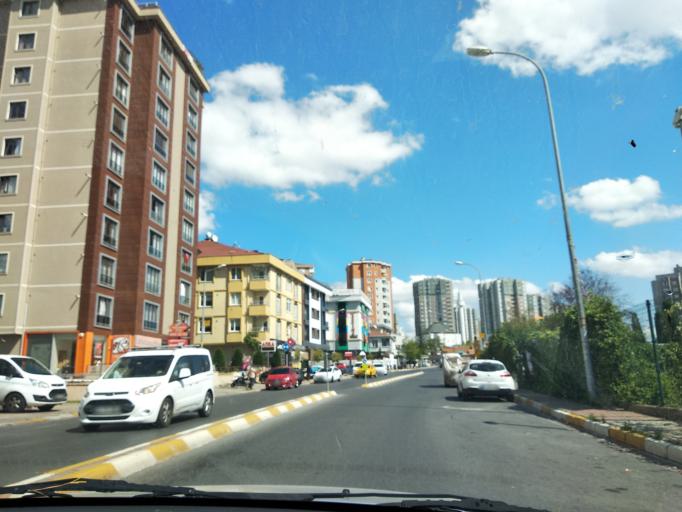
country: TR
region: Istanbul
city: Umraniye
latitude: 41.0087
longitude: 29.1104
